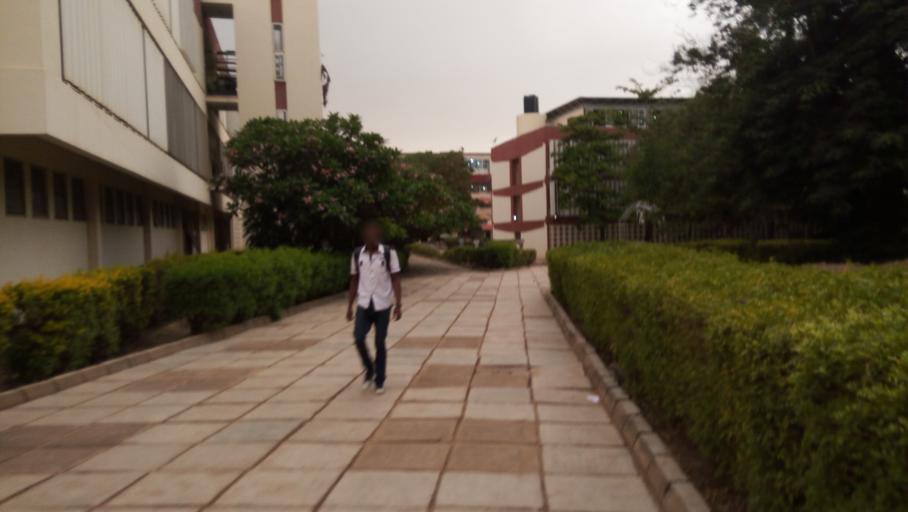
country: NG
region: Kaduna
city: Zaria
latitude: 11.1521
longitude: 7.6513
